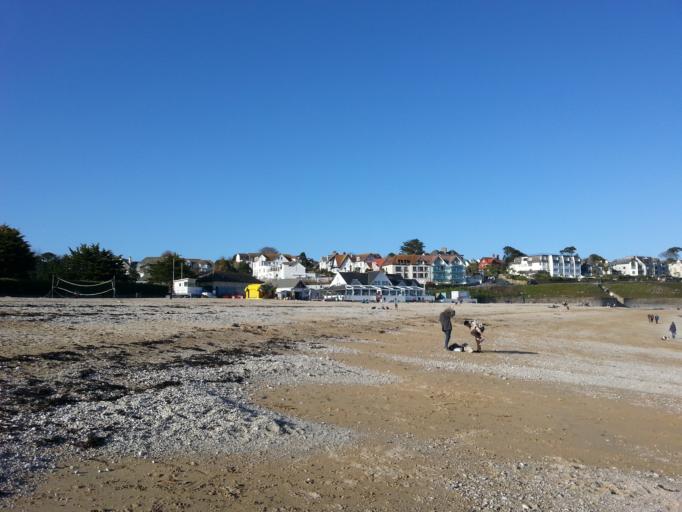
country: GB
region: England
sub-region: Cornwall
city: Falmouth
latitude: 50.1435
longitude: -5.0688
